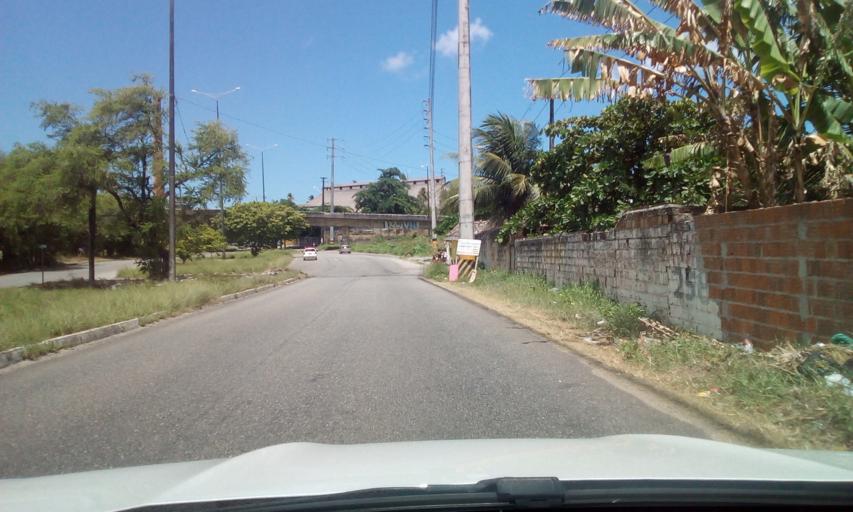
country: BR
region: Paraiba
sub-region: Joao Pessoa
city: Joao Pessoa
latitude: -7.1244
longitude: -34.8946
